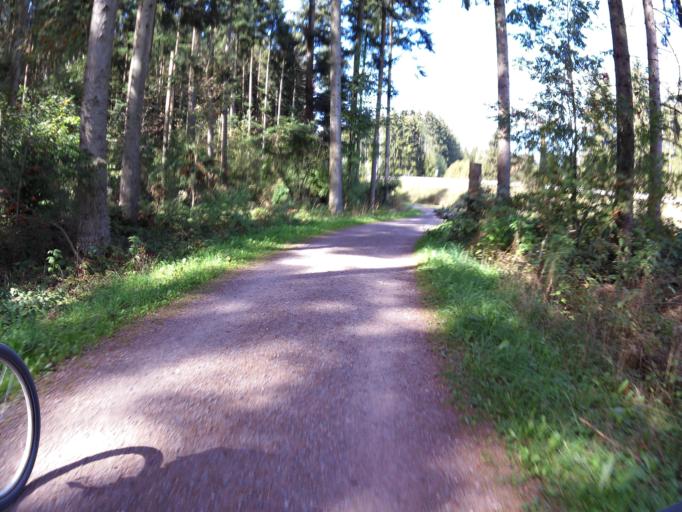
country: DE
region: Baden-Wuerttemberg
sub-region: Freiburg Region
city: Bad Durrheim
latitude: 48.0444
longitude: 8.5171
